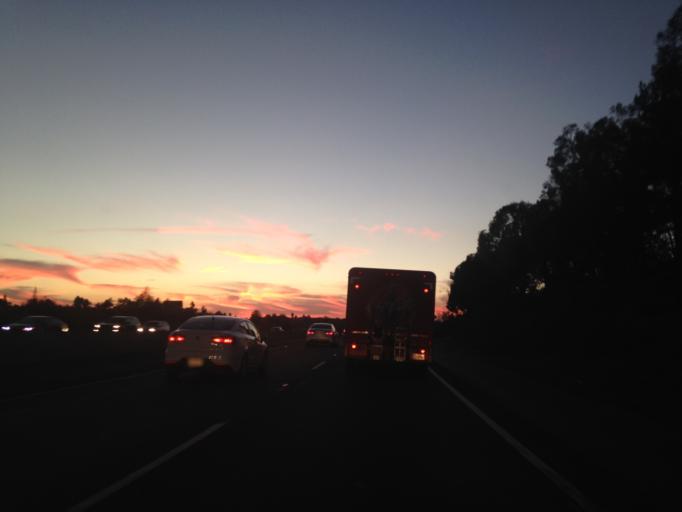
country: US
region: California
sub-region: San Diego County
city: Vista
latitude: 33.2483
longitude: -117.2756
